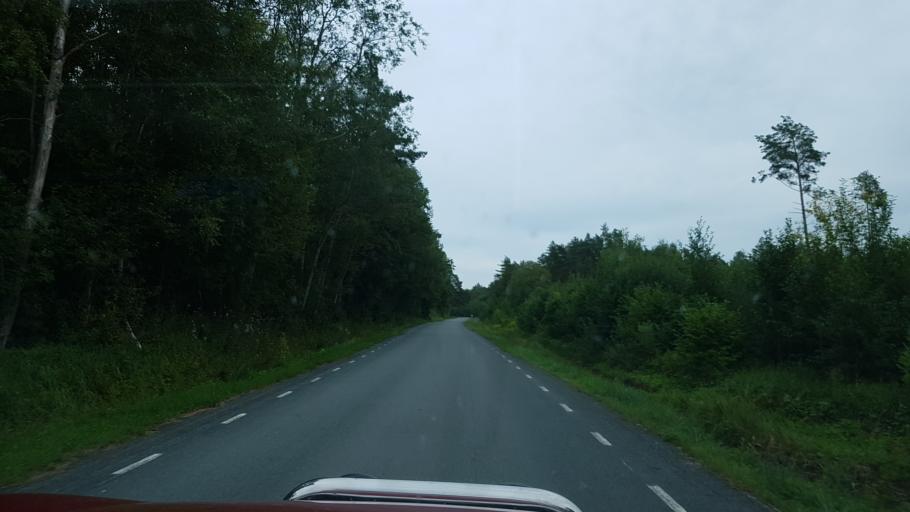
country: EE
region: Laeaene
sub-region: Lihula vald
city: Lihula
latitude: 58.8715
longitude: 23.9187
